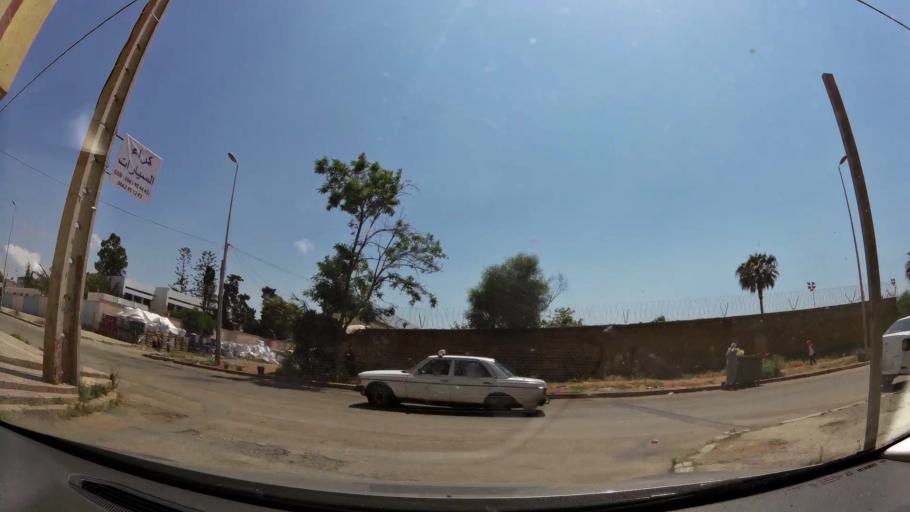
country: MA
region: Rabat-Sale-Zemmour-Zaer
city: Sale
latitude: 34.0412
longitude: -6.7946
